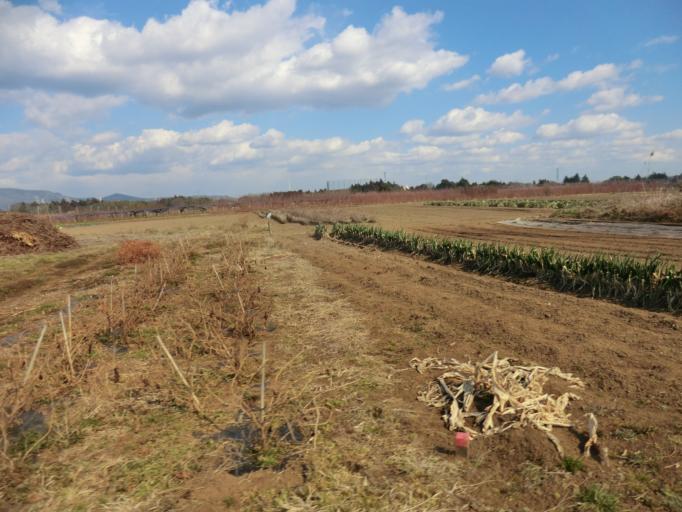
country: JP
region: Ibaraki
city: Naka
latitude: 36.1101
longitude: 140.1668
